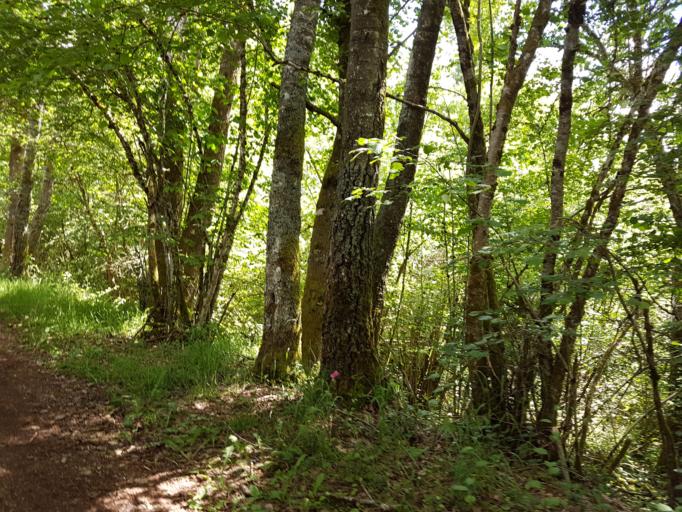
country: FR
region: Bourgogne
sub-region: Departement de la Cote-d'Or
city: Saulieu
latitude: 47.1798
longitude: 4.0872
